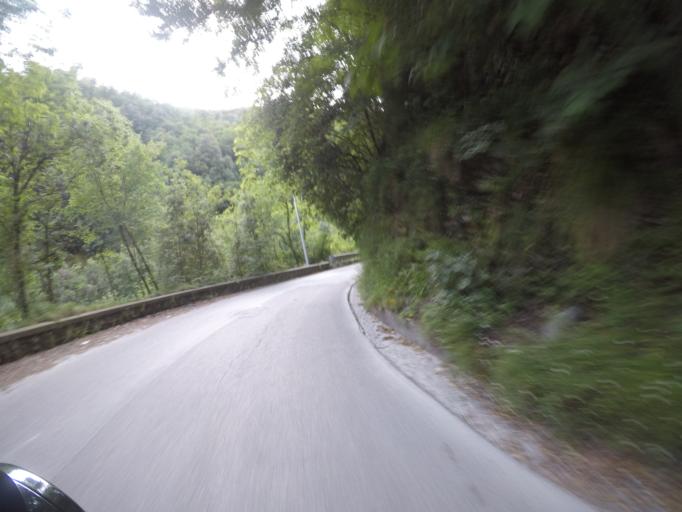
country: IT
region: Tuscany
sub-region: Provincia di Massa-Carrara
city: Carrara
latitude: 44.0953
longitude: 10.1033
